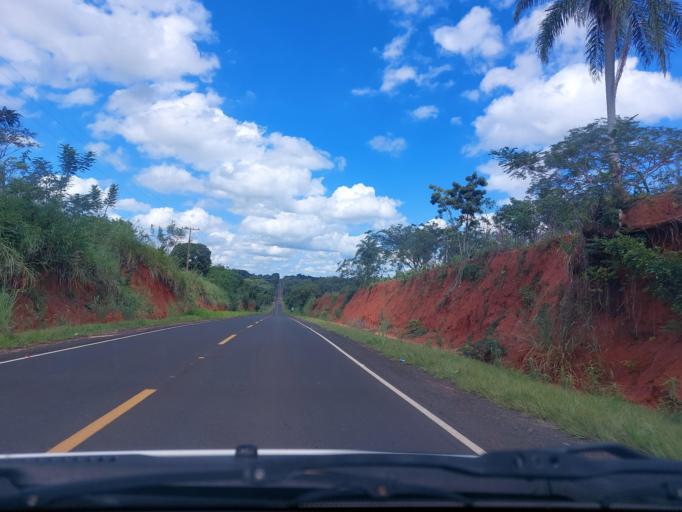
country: PY
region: San Pedro
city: Guayaybi
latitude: -24.5443
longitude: -56.5196
